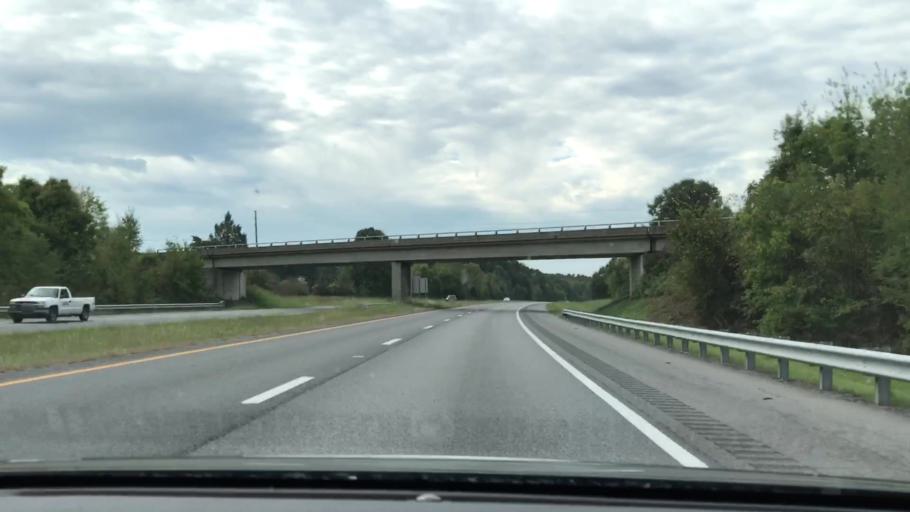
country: US
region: Kentucky
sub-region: Marshall County
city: Benton
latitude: 36.9022
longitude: -88.3475
